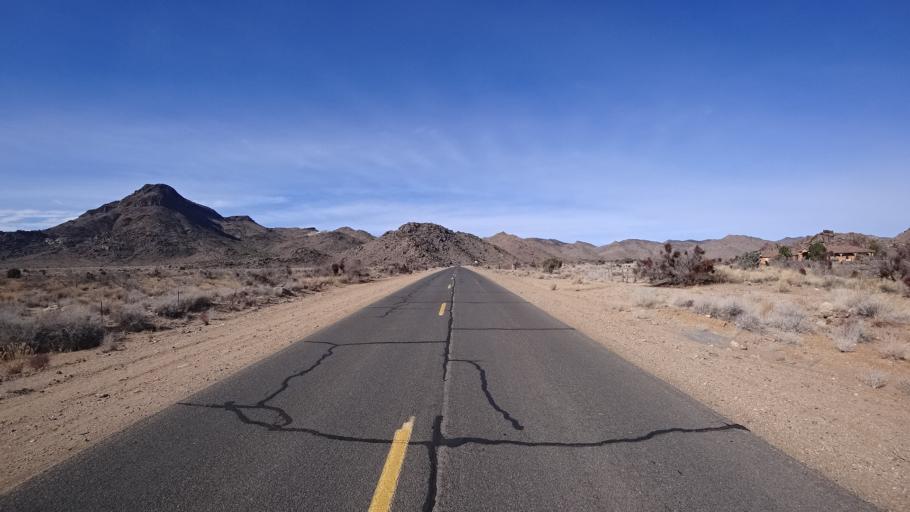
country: US
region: Arizona
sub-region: Mohave County
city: New Kingman-Butler
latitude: 35.2877
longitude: -114.0510
